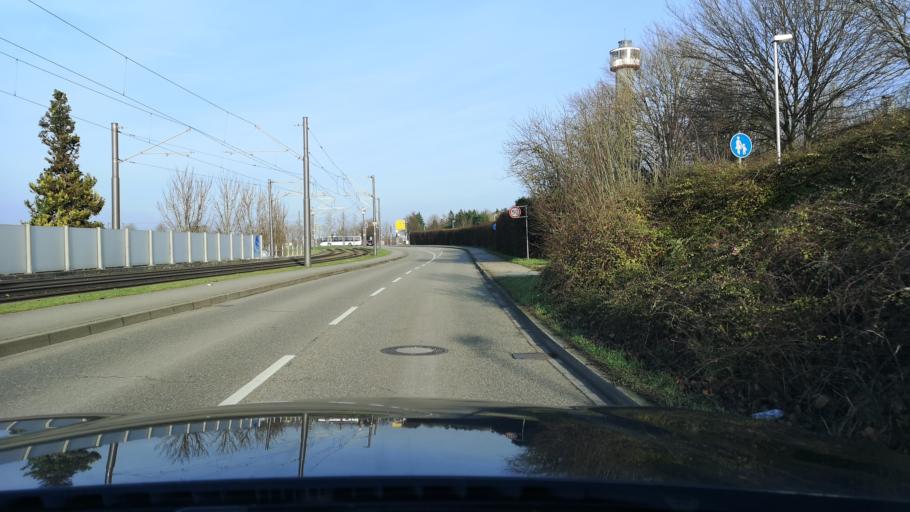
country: DE
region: Baden-Wuerttemberg
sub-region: Karlsruhe Region
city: Karlsruhe
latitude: 48.9808
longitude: 8.4604
